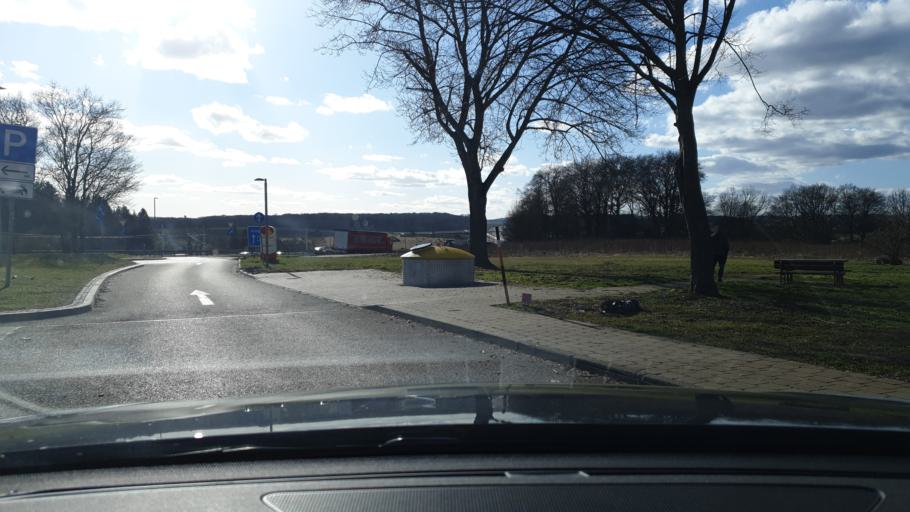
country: DE
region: Baden-Wuerttemberg
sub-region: Tuebingen Region
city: Nellingen
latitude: 48.5208
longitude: 9.8057
